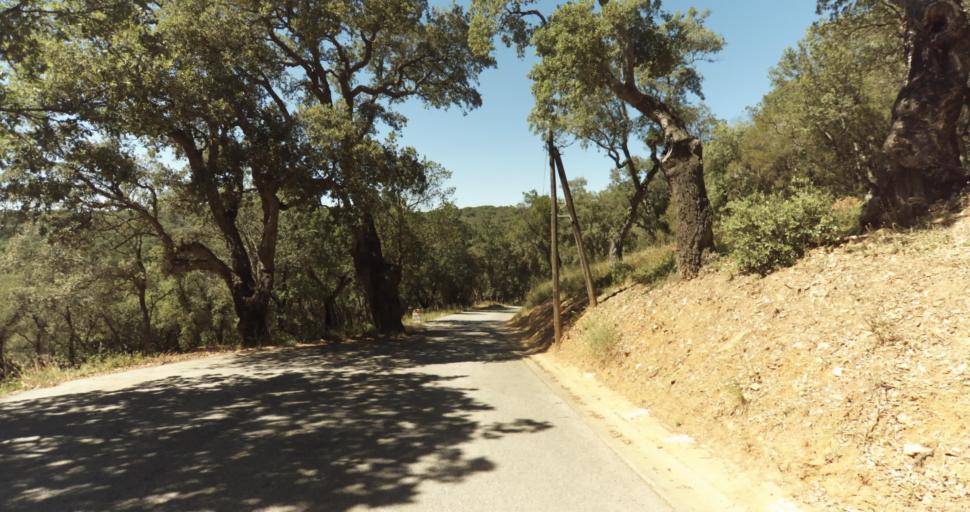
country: FR
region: Provence-Alpes-Cote d'Azur
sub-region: Departement du Var
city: La Croix-Valmer
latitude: 43.2271
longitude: 6.5603
